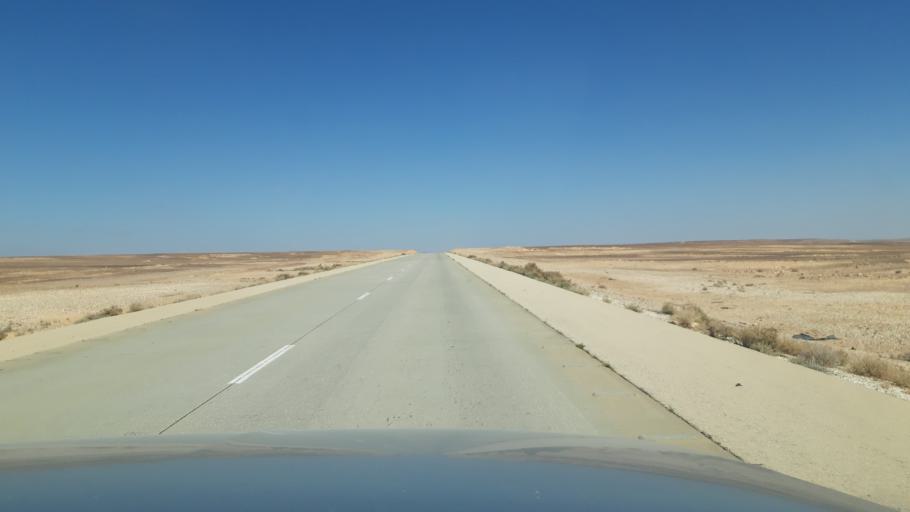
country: SA
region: Al Jawf
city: Al Qurayyat
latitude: 31.0940
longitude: 36.6360
